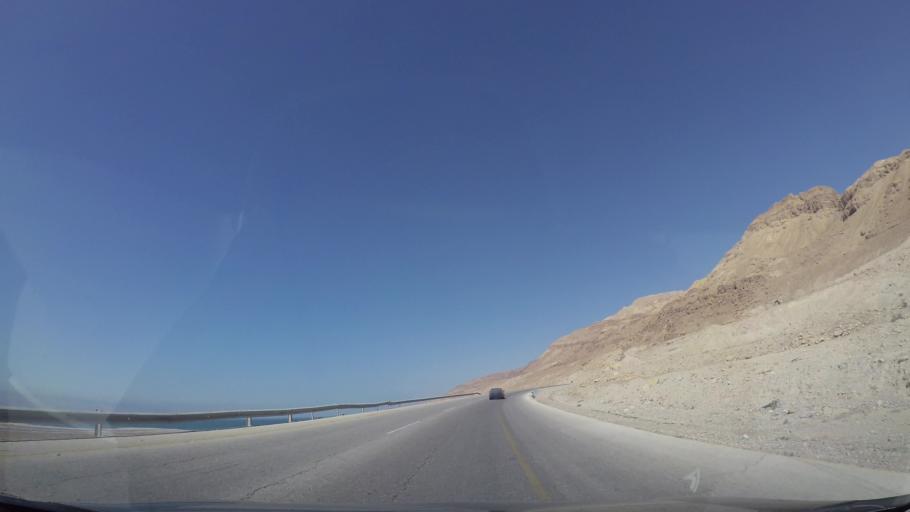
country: JO
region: Karak
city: Al Qasr
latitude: 31.3291
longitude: 35.5451
